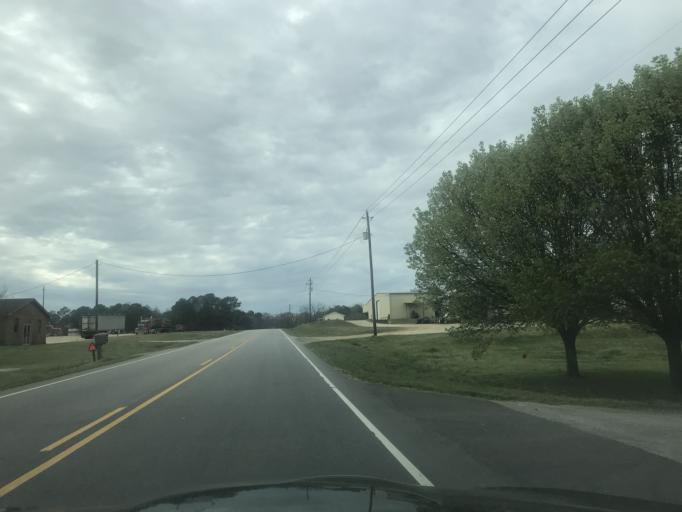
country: US
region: North Carolina
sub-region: Franklin County
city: Louisburg
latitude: 36.0882
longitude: -78.3626
